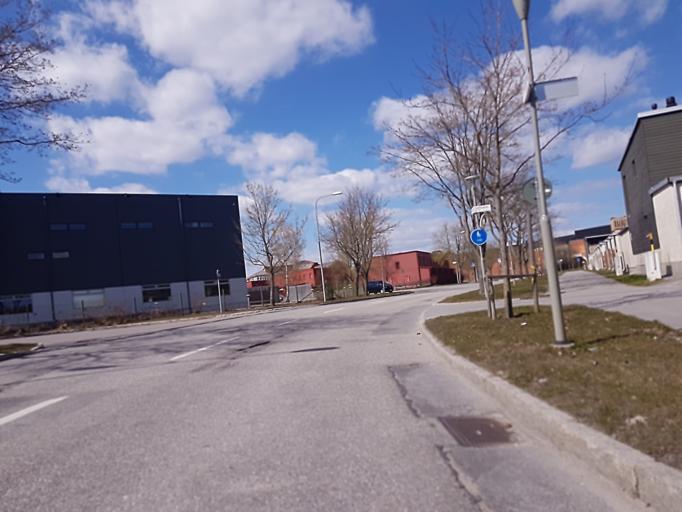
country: SE
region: Stockholm
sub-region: Nacka Kommun
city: Alta
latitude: 59.2625
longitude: 18.1330
